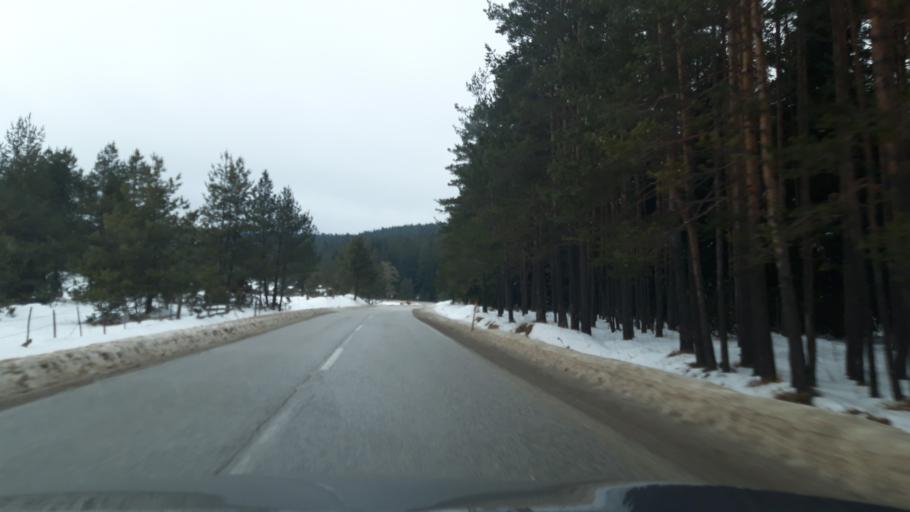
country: BA
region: Republika Srpska
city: Sokolac
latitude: 43.9139
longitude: 18.7014
